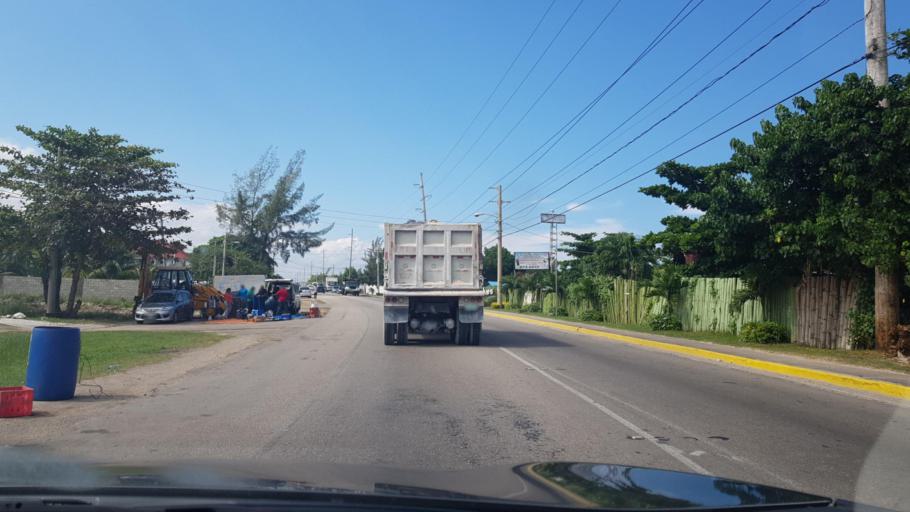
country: JM
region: Saint Ann
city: Runaway Bay
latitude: 18.4682
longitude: -77.2989
